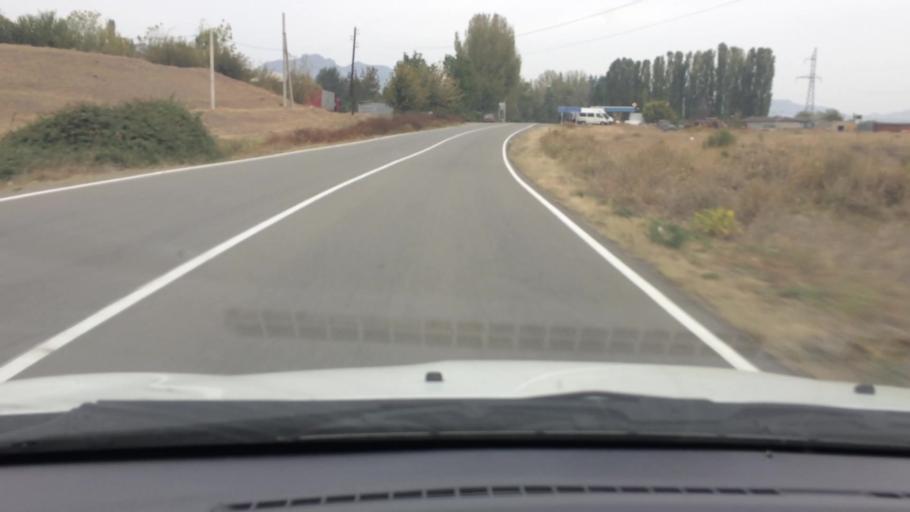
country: AM
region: Tavush
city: Bagratashen
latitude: 41.2901
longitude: 44.7883
